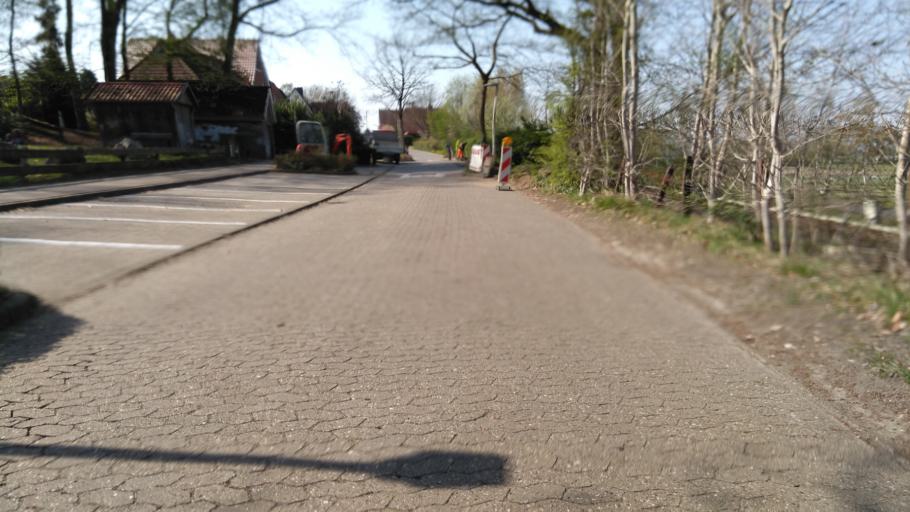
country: DE
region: Lower Saxony
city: Nottensdorf
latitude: 53.4798
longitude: 9.6430
